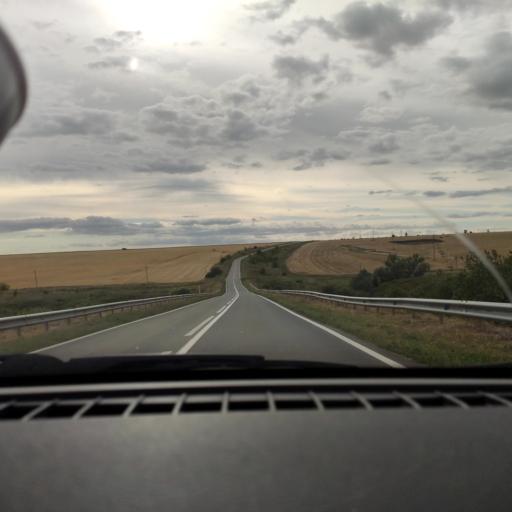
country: RU
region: Samara
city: Georgiyevka
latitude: 53.4163
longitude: 50.8811
